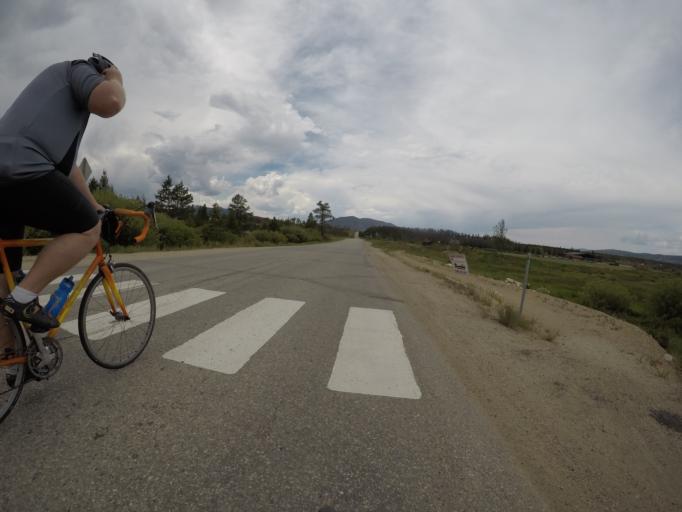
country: US
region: Colorado
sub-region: Grand County
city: Fraser
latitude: 39.9555
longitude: -105.8207
